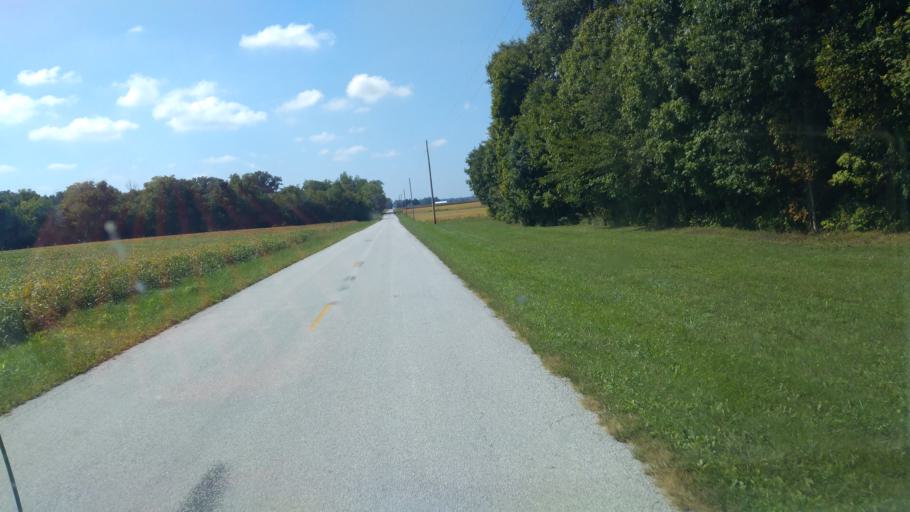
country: US
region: Ohio
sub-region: Hardin County
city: Ada
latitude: 40.7473
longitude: -83.7191
